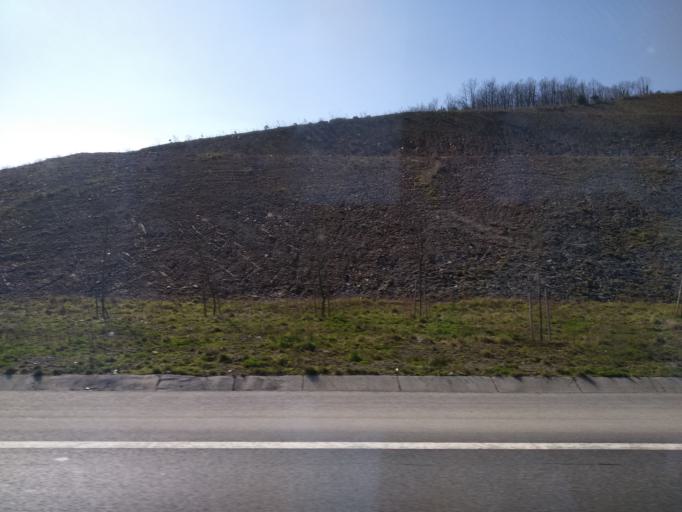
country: TR
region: Istanbul
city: Mahmut Sevket Pasa
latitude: 41.1567
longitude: 29.2647
